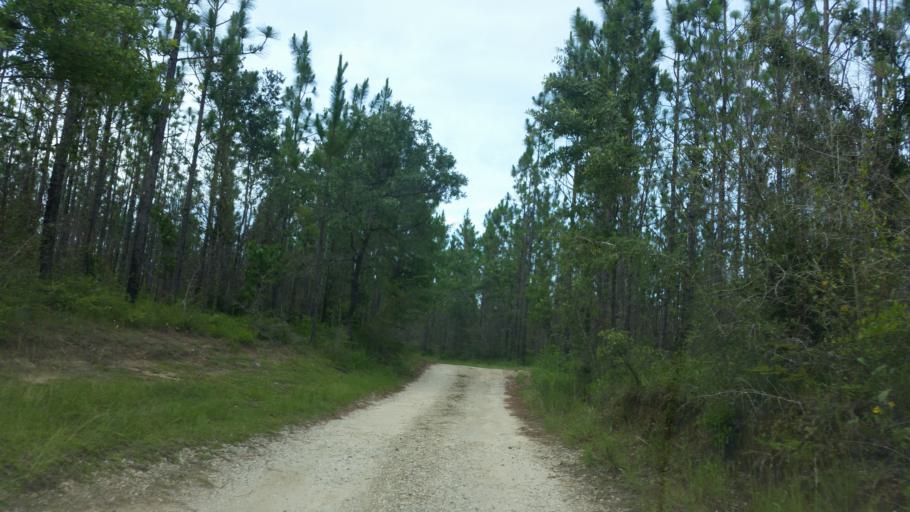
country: US
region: Florida
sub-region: Escambia County
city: Cantonment
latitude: 30.6321
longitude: -87.3899
